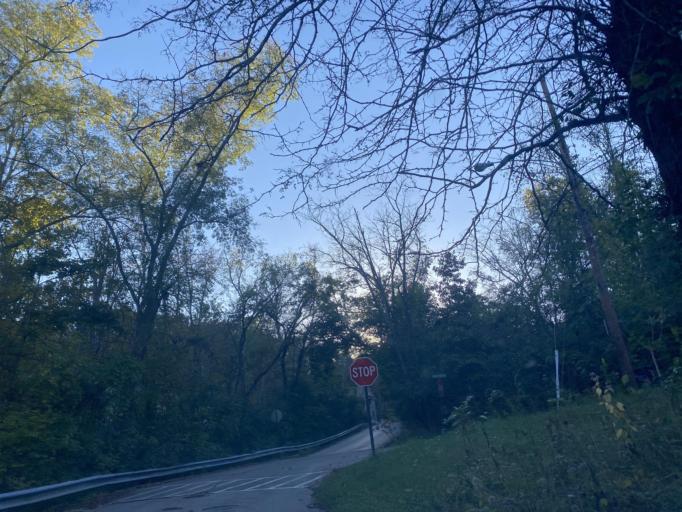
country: US
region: Kentucky
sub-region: Campbell County
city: Fort Thomas
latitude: 39.0951
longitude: -84.4430
